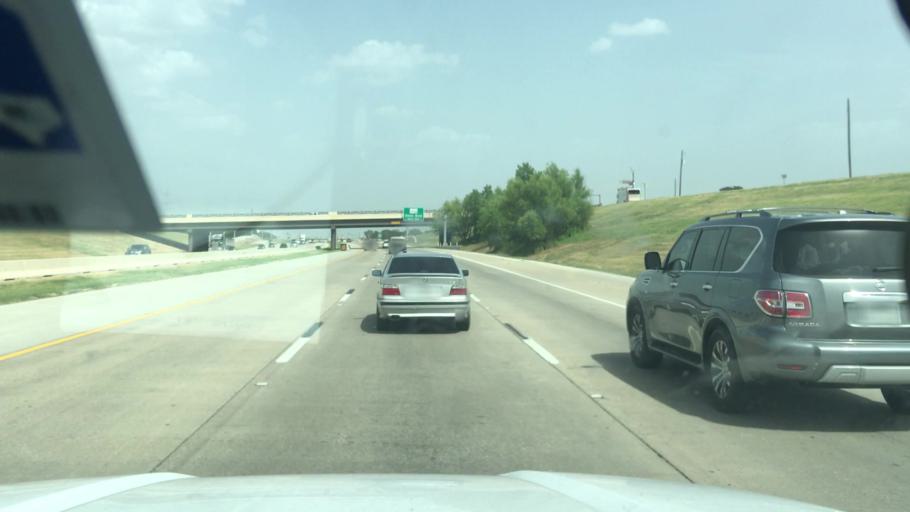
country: US
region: Texas
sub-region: Denton County
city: Trophy Club
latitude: 32.9931
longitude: -97.1945
